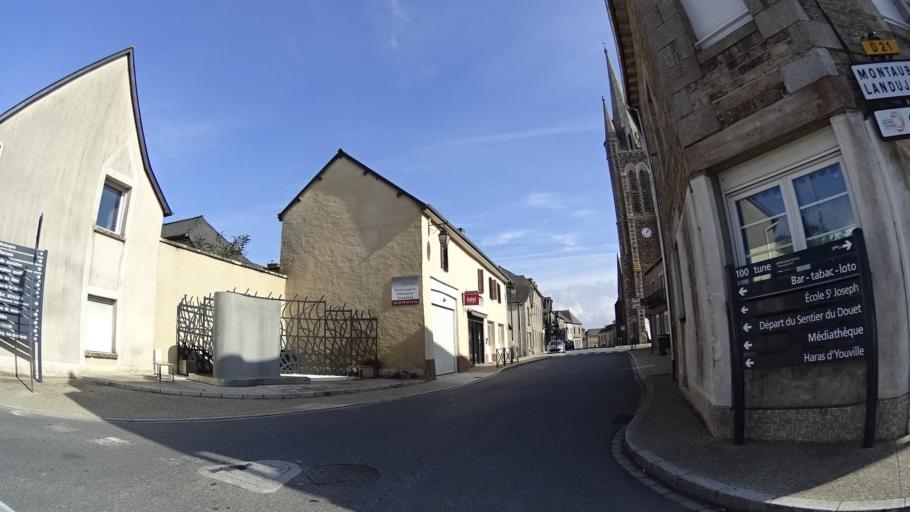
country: FR
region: Brittany
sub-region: Departement d'Ille-et-Vilaine
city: Medreac
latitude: 48.2676
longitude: -2.0665
